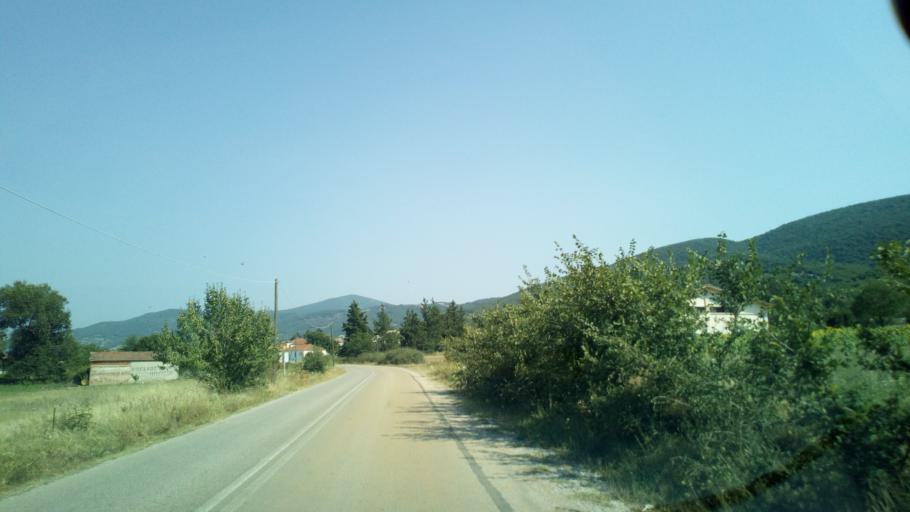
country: GR
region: Central Macedonia
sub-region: Nomos Chalkidikis
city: Galatista
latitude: 40.5089
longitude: 23.3720
